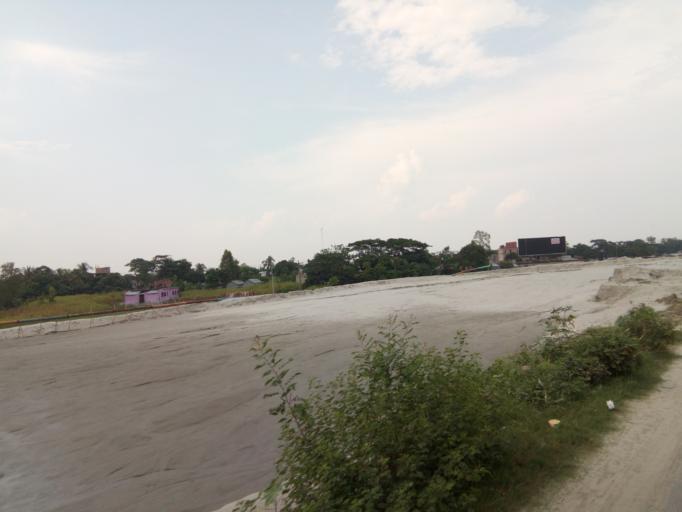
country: BD
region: Dhaka
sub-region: Dhaka
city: Dhaka
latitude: 23.6136
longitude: 90.3306
